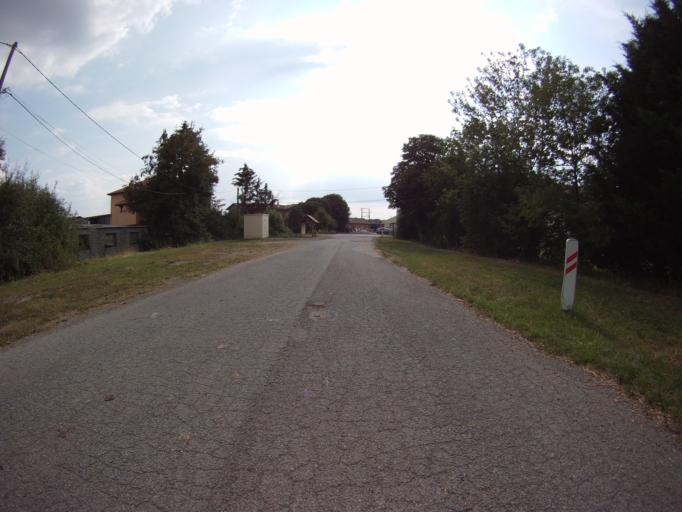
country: FR
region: Lorraine
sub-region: Departement de la Moselle
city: Mecleuves
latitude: 49.0642
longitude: 6.3120
